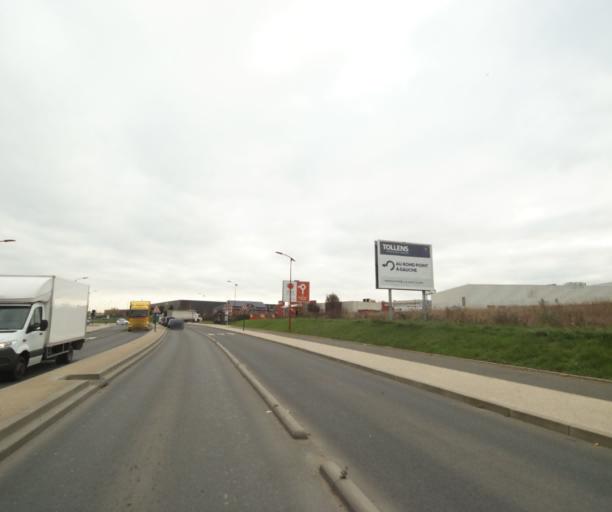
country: FR
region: Ile-de-France
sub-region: Departement du Val-d'Oise
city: Gonesse
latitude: 48.9825
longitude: 2.4421
